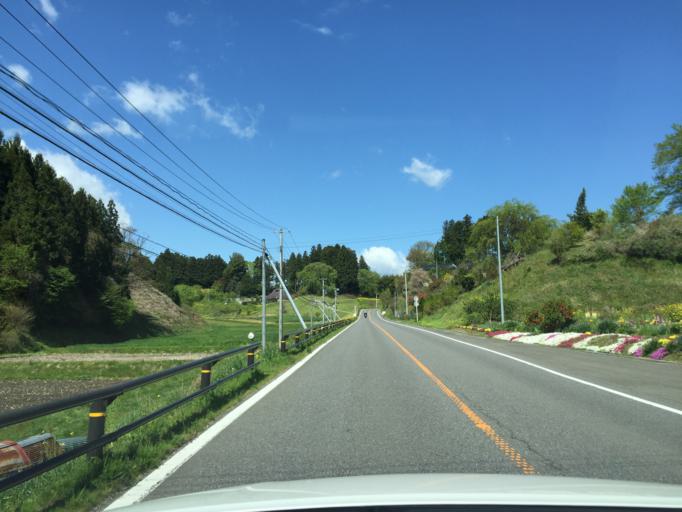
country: JP
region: Fukushima
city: Funehikimachi-funehiki
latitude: 37.5375
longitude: 140.5837
